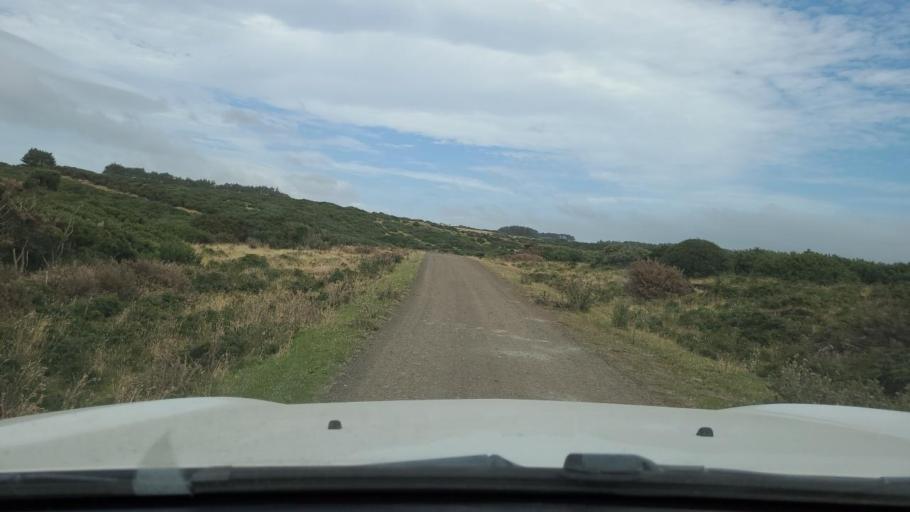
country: NZ
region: Chatham Islands
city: Waitangi
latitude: -43.9579
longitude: -176.4818
